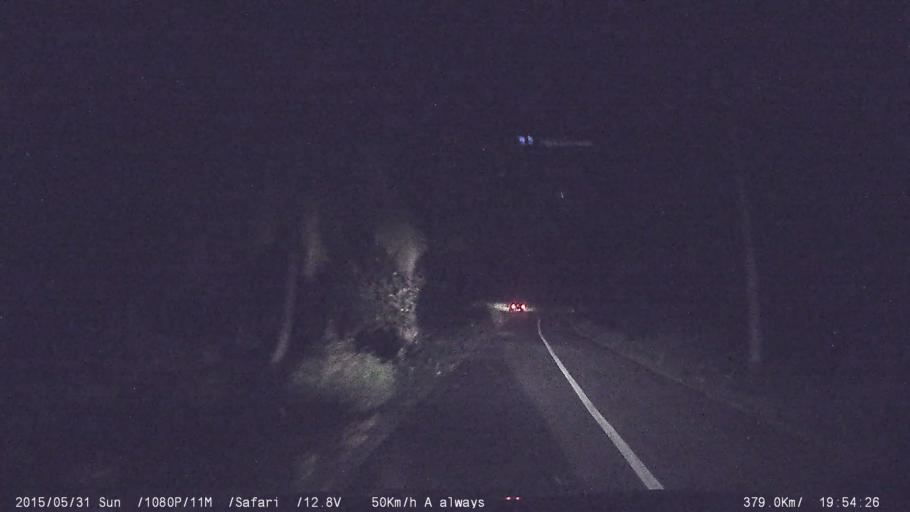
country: IN
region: Karnataka
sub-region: Mandya
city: Malavalli
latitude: 12.3555
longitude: 77.0739
